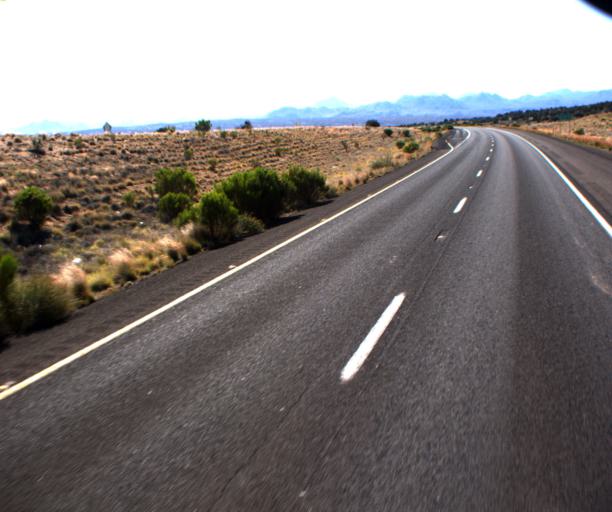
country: US
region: Arizona
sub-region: Mohave County
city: New Kingman-Butler
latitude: 35.1456
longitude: -113.6856
